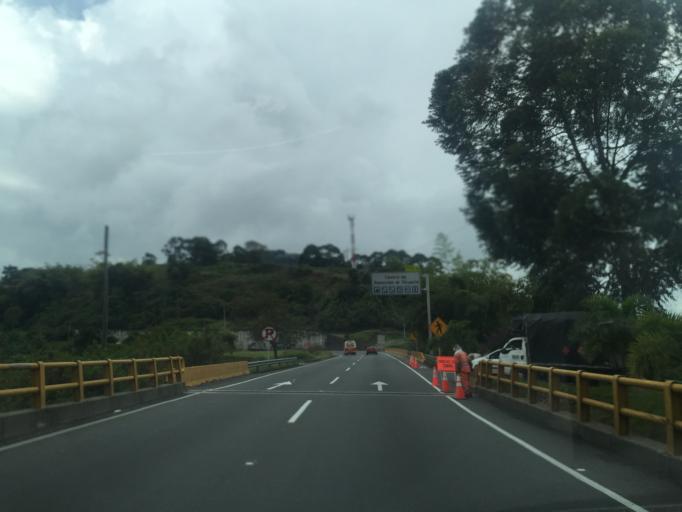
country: CO
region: Risaralda
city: Santa Rosa de Cabal
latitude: 4.8536
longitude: -75.6409
